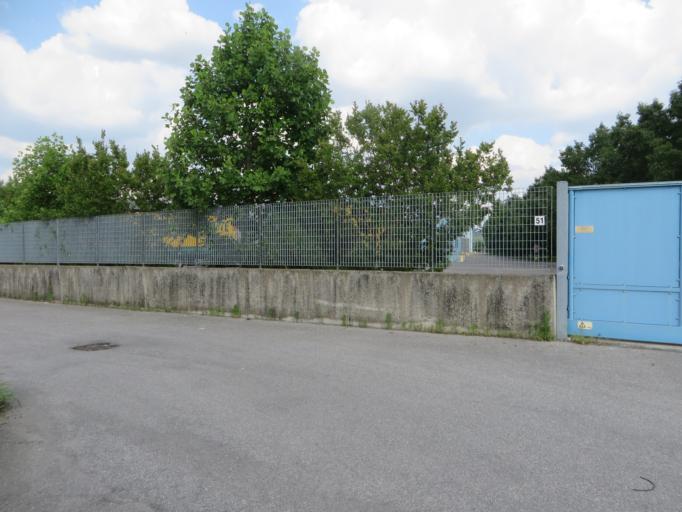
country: IT
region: Lombardy
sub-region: Provincia di Brescia
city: Cologne
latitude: 45.5686
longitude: 9.9481
